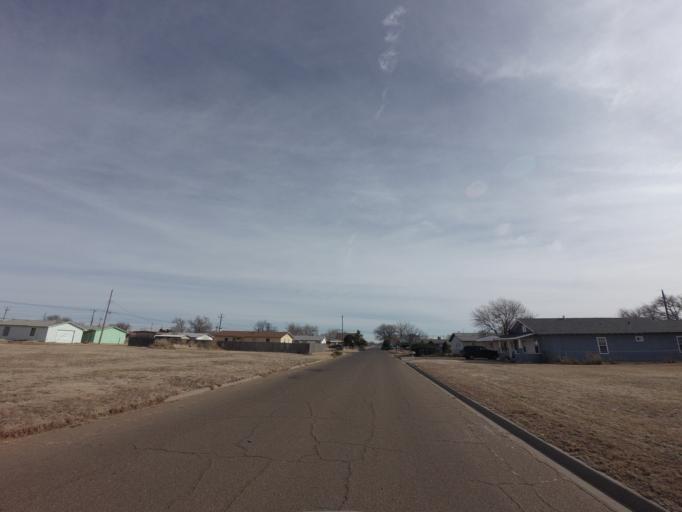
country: US
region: New Mexico
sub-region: Curry County
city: Clovis
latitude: 34.4098
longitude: -103.2456
